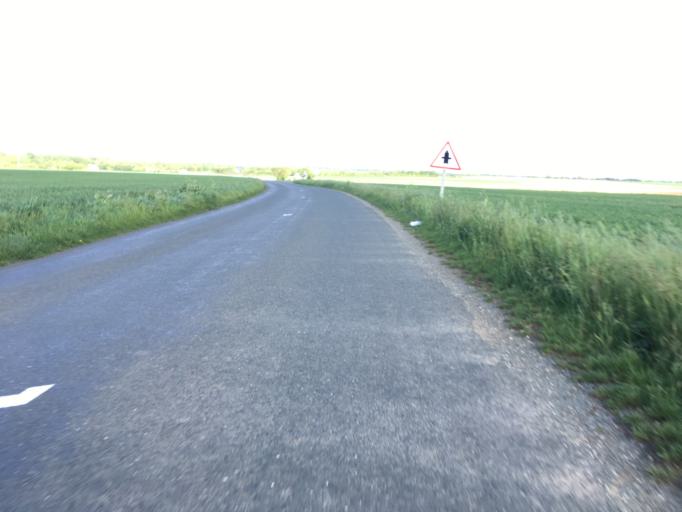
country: FR
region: Poitou-Charentes
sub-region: Departement de la Charente-Maritime
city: Verines
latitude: 46.1703
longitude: -0.8959
